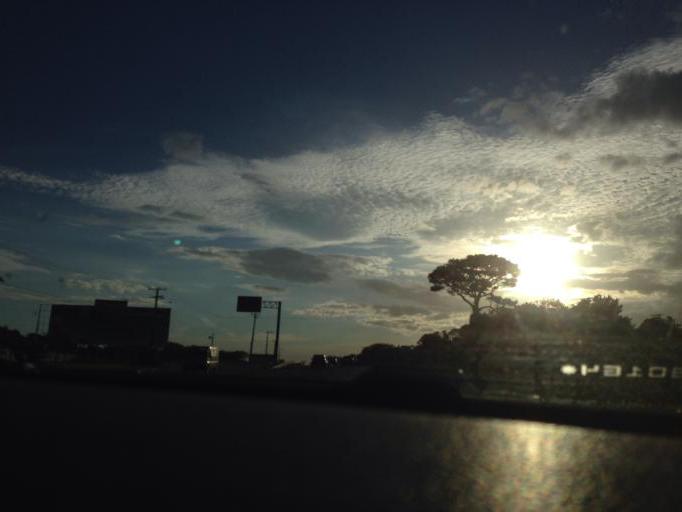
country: BR
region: Espirito Santo
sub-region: Guarapari
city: Guarapari
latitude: -20.5279
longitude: -40.3804
